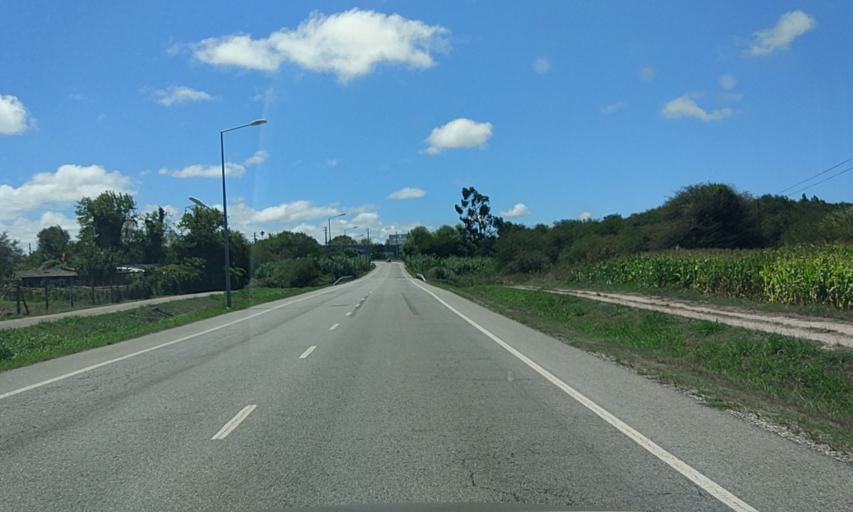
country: PT
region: Aveiro
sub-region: Ilhavo
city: Ilhavo
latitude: 40.5958
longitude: -8.6799
